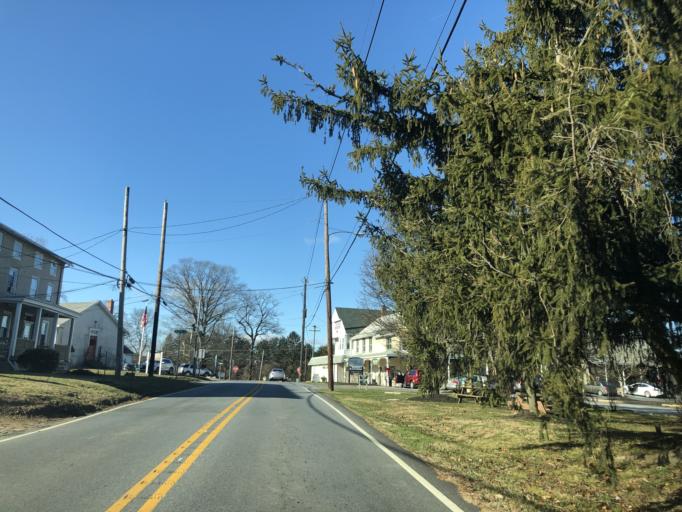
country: US
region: Pennsylvania
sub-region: Chester County
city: South Coatesville
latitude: 39.9462
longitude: -75.8380
